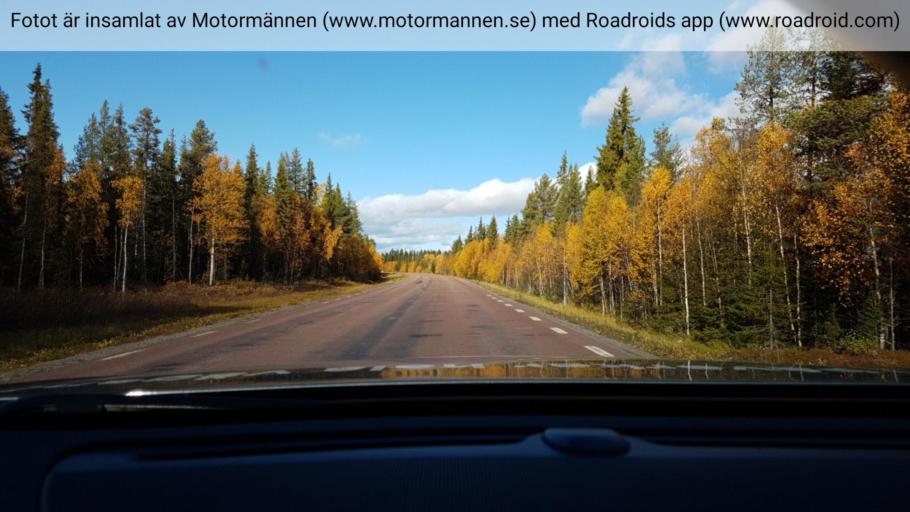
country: SE
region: Norrbotten
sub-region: Arjeplogs Kommun
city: Arjeplog
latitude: 65.9861
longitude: 18.1895
